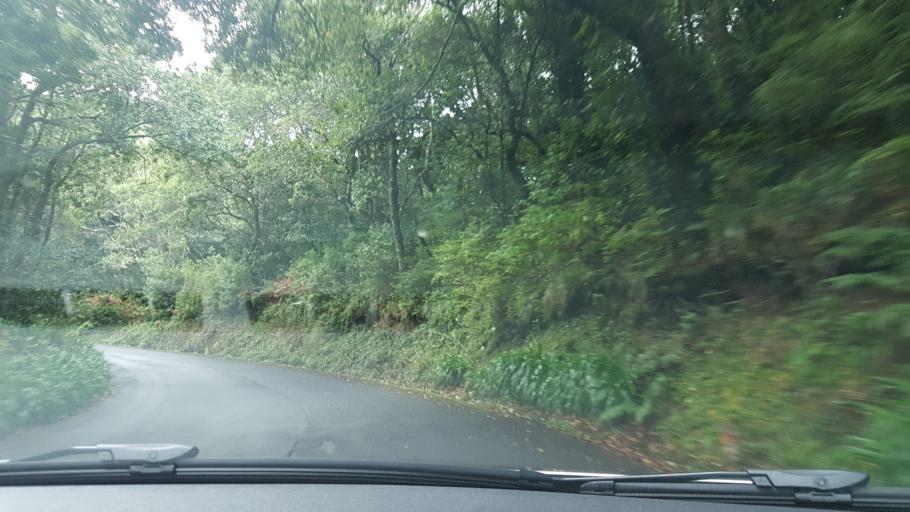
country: PT
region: Madeira
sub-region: Sao Vicente
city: Sao Vicente
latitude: 32.7595
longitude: -17.0184
